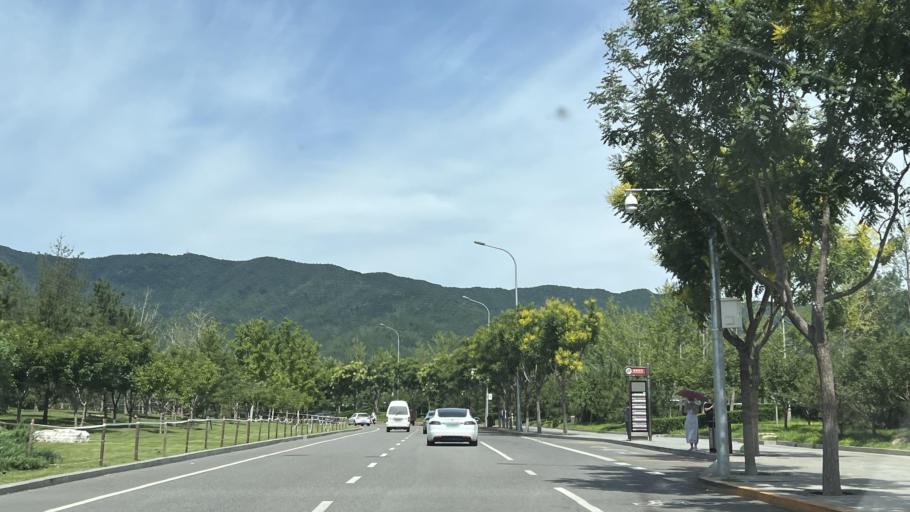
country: CN
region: Beijing
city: Xiangshan
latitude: 39.9920
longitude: 116.2146
